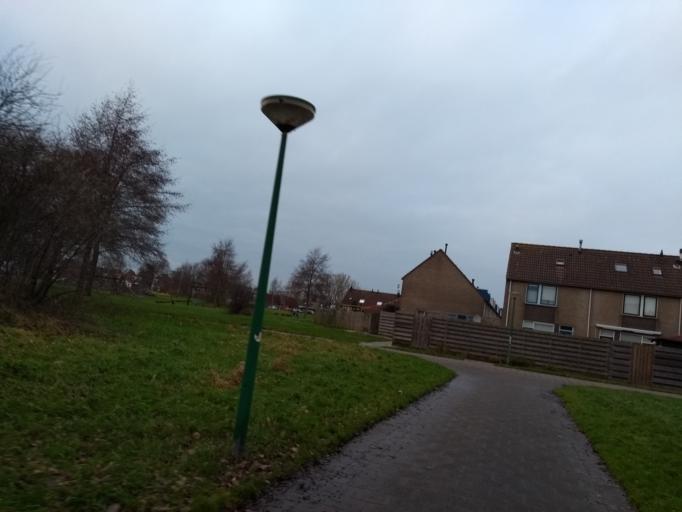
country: NL
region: Friesland
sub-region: Sudwest Fryslan
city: Sneek
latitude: 53.0184
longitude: 5.6654
